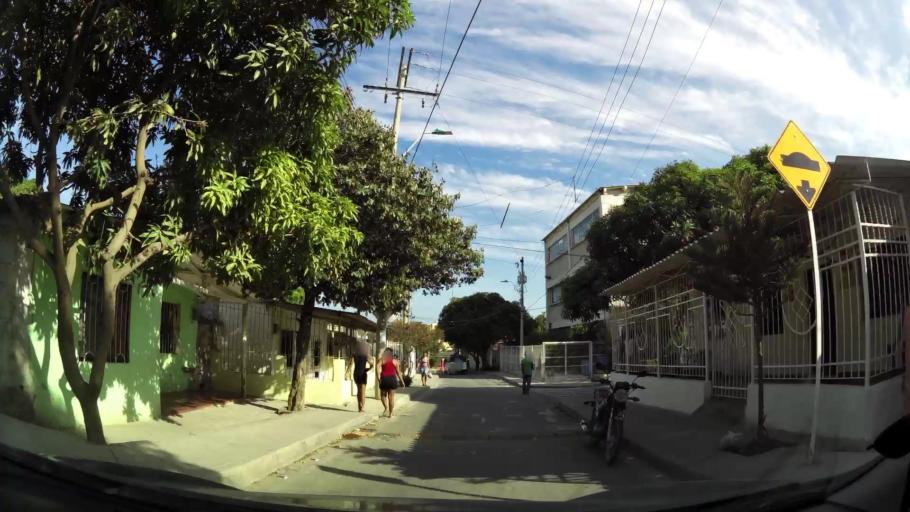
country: CO
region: Atlantico
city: Soledad
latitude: 10.9258
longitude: -74.8120
